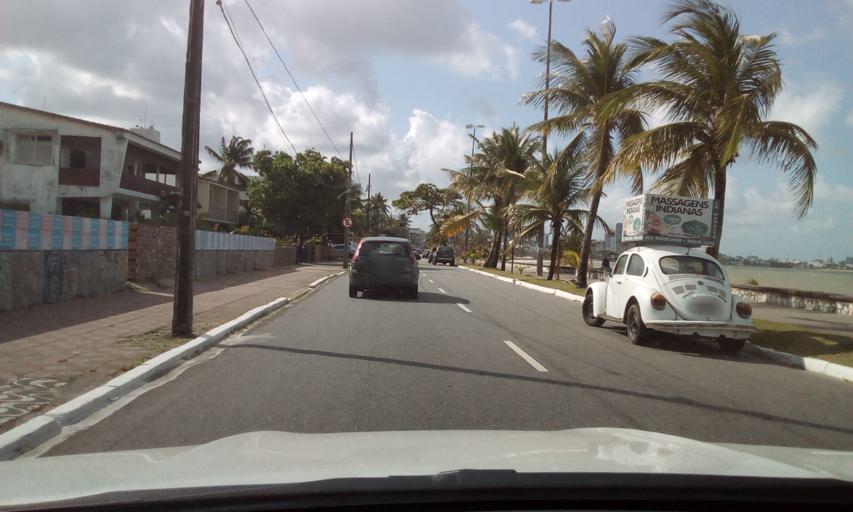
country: BR
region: Paraiba
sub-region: Joao Pessoa
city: Joao Pessoa
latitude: -7.1046
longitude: -34.8297
